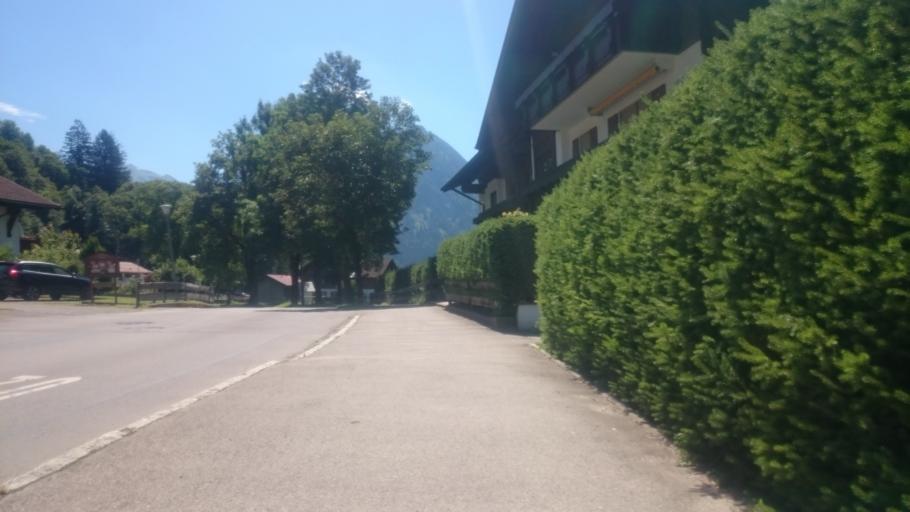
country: DE
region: Bavaria
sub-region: Swabia
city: Oberstdorf
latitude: 47.3999
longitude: 10.2795
